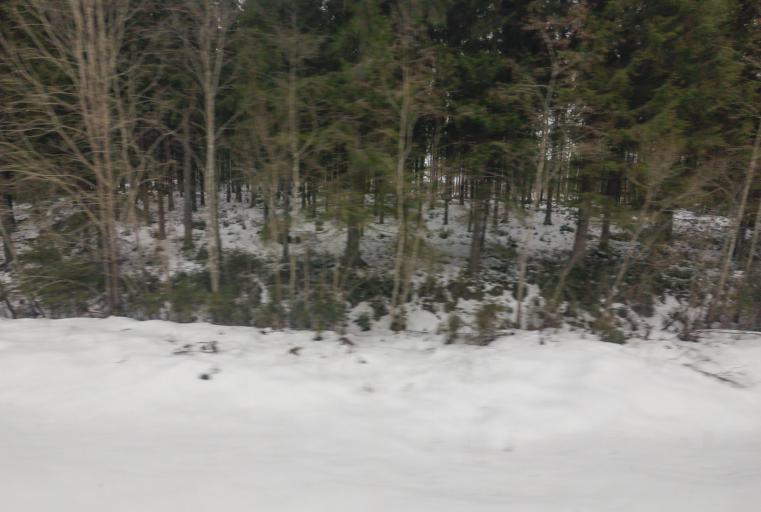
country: FI
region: Southern Savonia
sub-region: Savonlinna
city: Savonlinna
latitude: 61.8573
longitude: 28.9803
